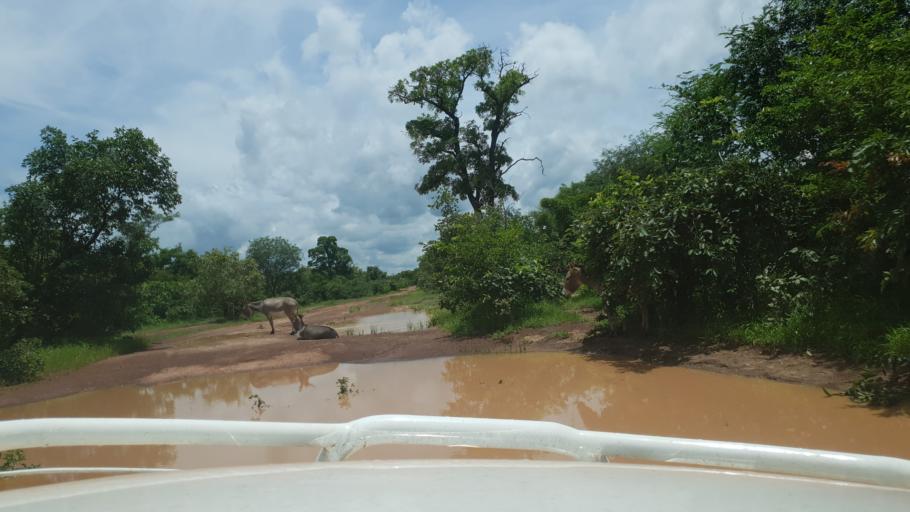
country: ML
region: Koulikoro
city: Banamba
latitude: 13.2009
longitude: -7.3379
